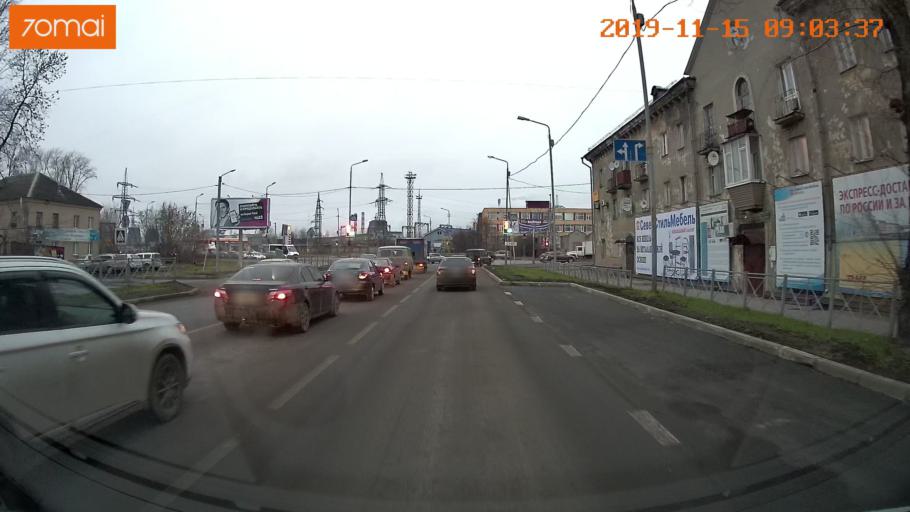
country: RU
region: Vologda
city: Cherepovets
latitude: 59.1392
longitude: 37.9199
